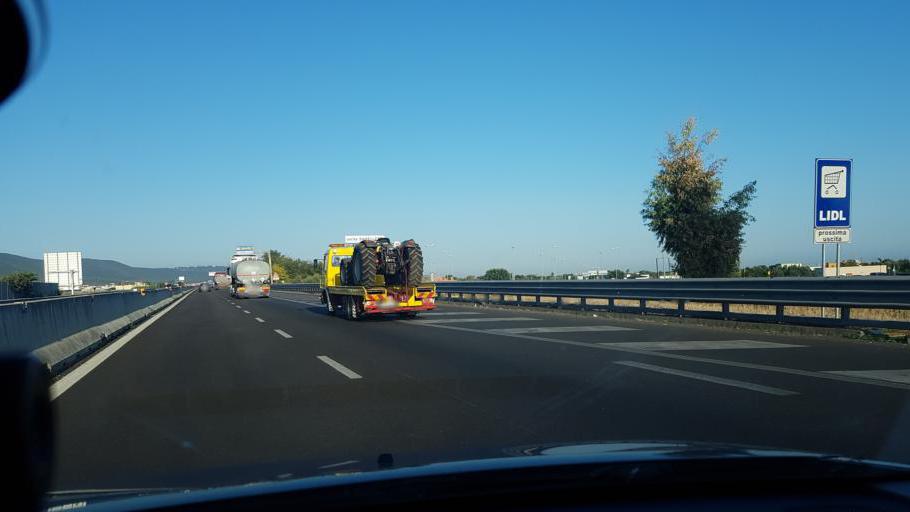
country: IT
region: Apulia
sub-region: Provincia di Brindisi
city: Fasano
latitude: 40.8385
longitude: 17.3784
